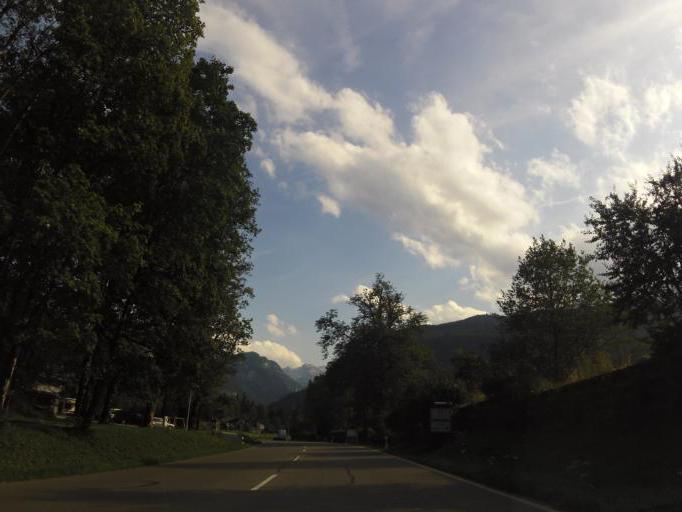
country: DE
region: Bavaria
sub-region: Upper Bavaria
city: Schoenau am Koenigssee
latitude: 47.6005
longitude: 12.9895
